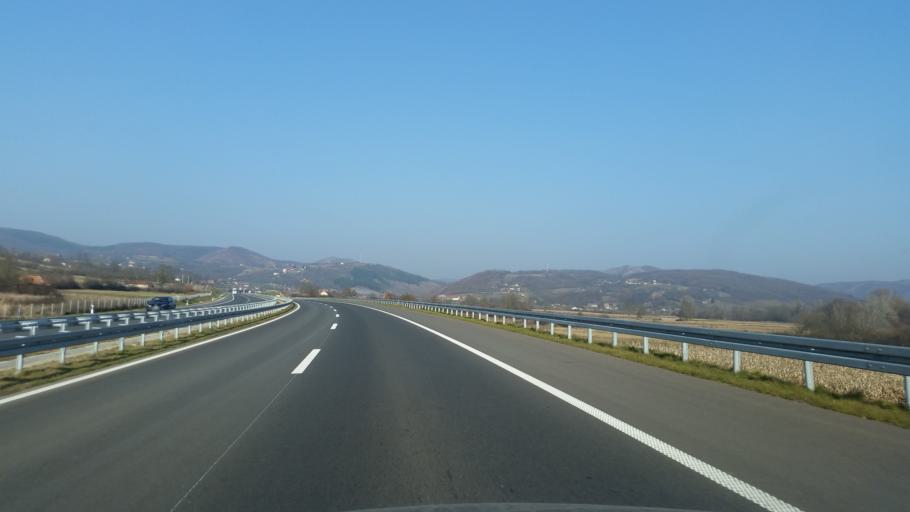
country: RS
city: Prislonica
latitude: 43.9516
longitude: 20.4009
